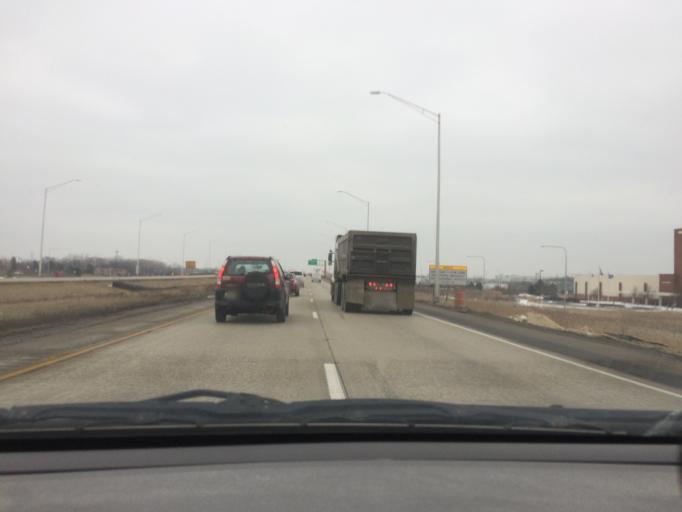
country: US
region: Illinois
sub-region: DuPage County
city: Roselle
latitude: 41.9970
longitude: -88.1066
